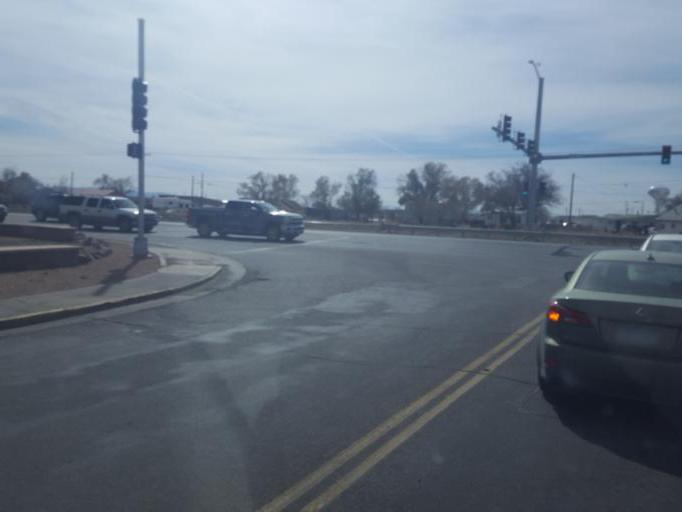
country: US
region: Colorado
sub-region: Alamosa County
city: Alamosa
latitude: 37.4731
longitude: -105.8889
